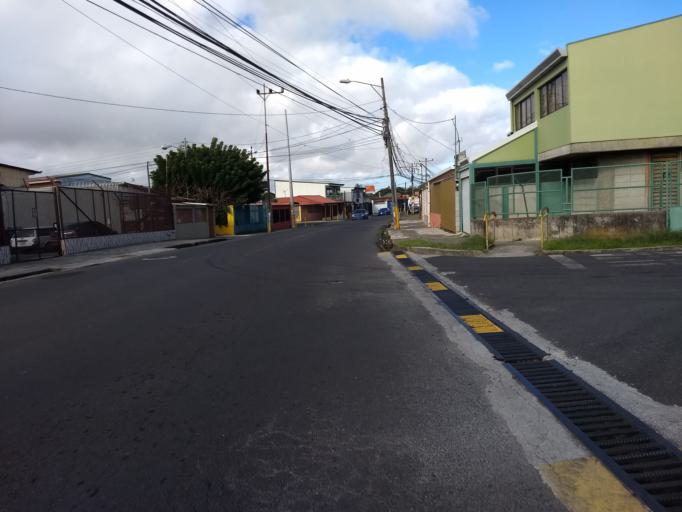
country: CR
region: San Jose
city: Calle Blancos
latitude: 9.9635
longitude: -84.0641
